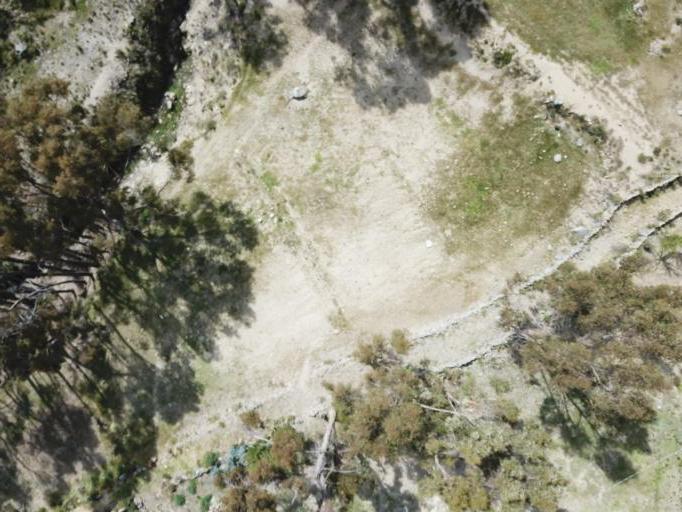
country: BO
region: La Paz
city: Achacachi
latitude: -16.0505
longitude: -68.8111
